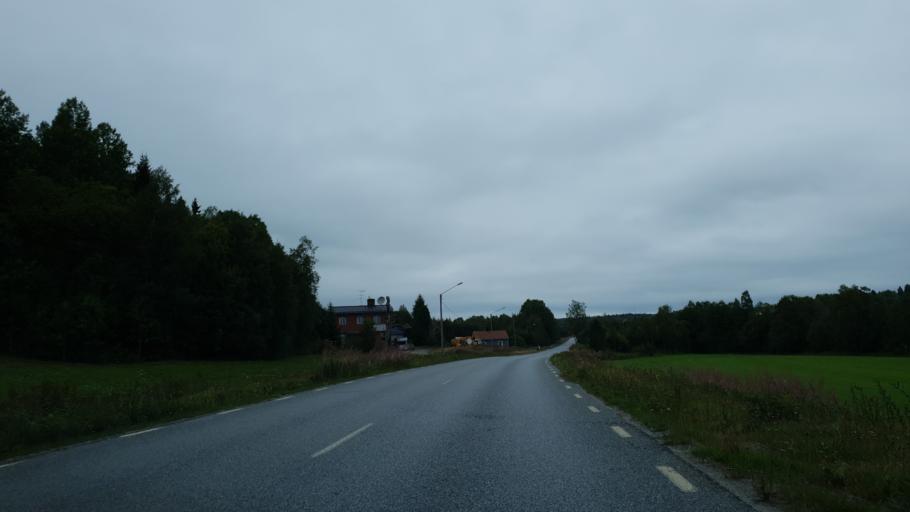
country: SE
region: Vaesterbotten
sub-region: Skelleftea Kommun
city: Burea
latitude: 64.3942
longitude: 21.2929
